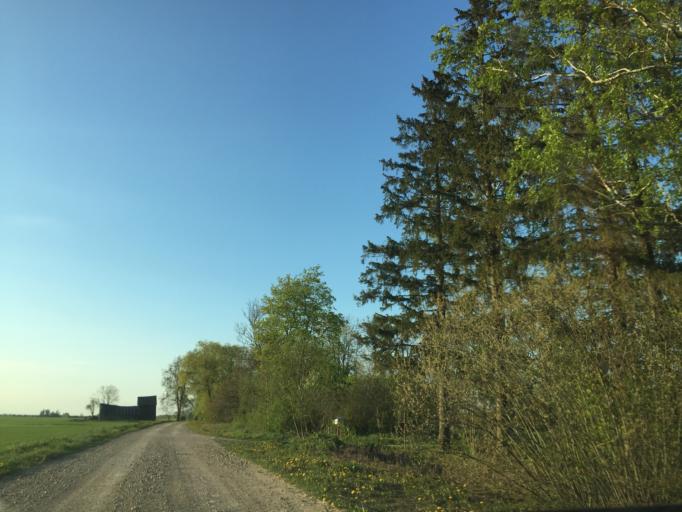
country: LV
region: Bauskas Rajons
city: Bauska
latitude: 56.3034
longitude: 24.1787
